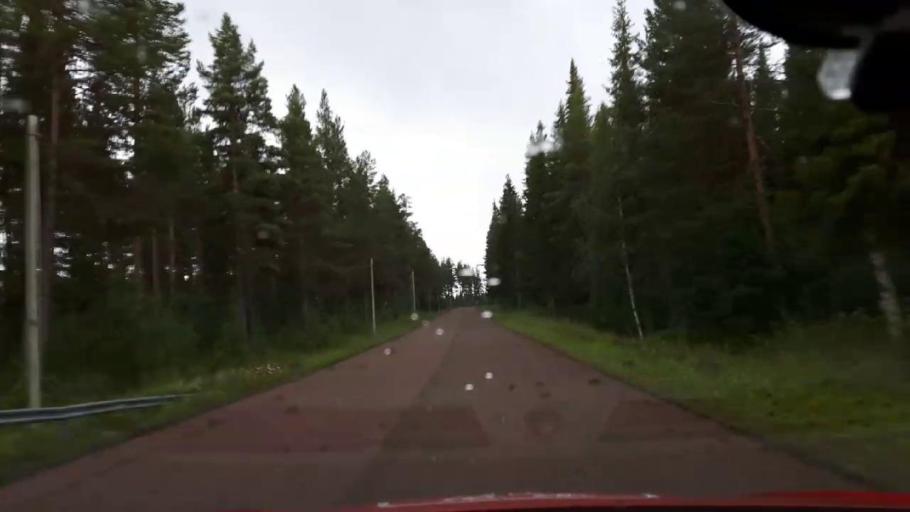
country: SE
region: Jaemtland
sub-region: Are Kommun
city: Jarpen
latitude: 63.3199
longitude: 13.6947
